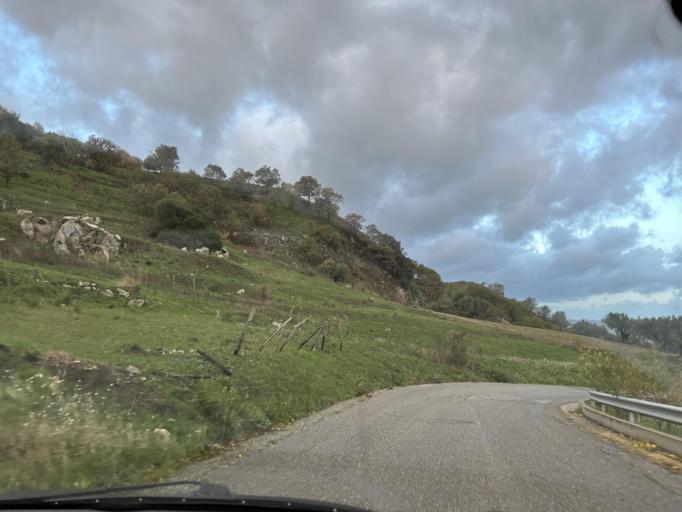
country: IT
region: Calabria
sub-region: Provincia di Catanzaro
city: Montauro
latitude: 38.7647
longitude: 16.5173
